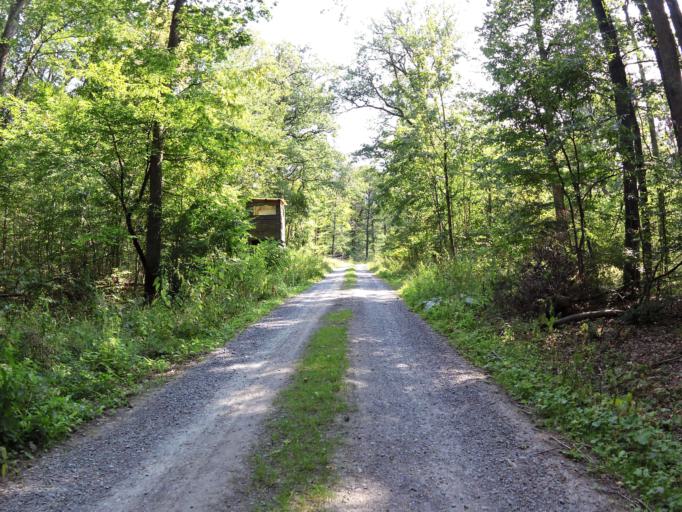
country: DE
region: Bavaria
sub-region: Regierungsbezirk Unterfranken
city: Waldbrunn
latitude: 49.7161
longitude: 9.8051
